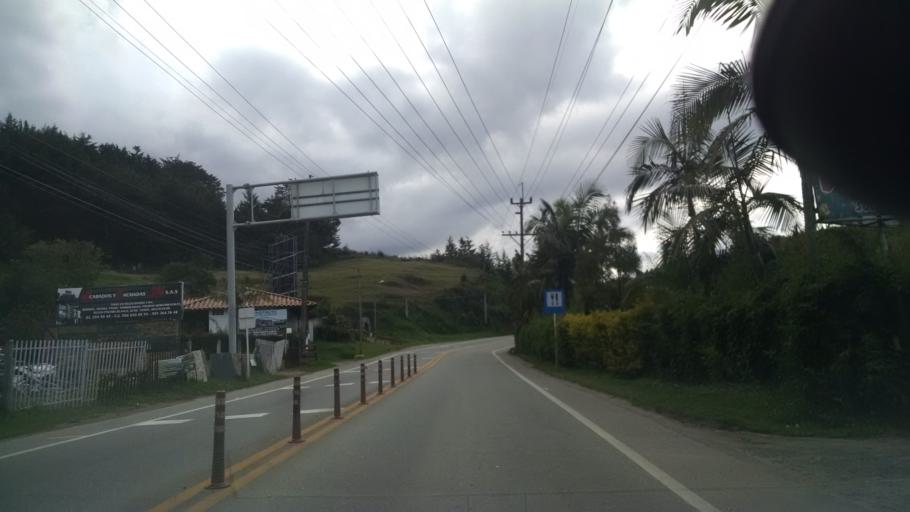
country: CO
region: Antioquia
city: El Retiro
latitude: 6.0911
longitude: -75.4810
